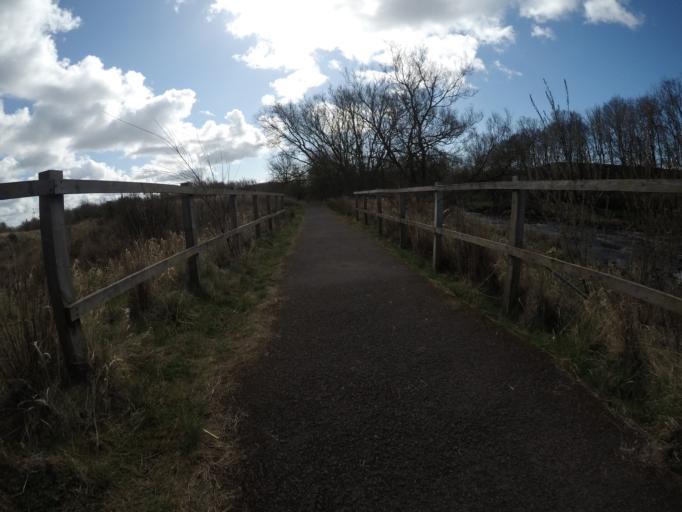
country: GB
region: Scotland
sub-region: North Ayrshire
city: Dreghorn
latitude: 55.5997
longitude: -4.6327
